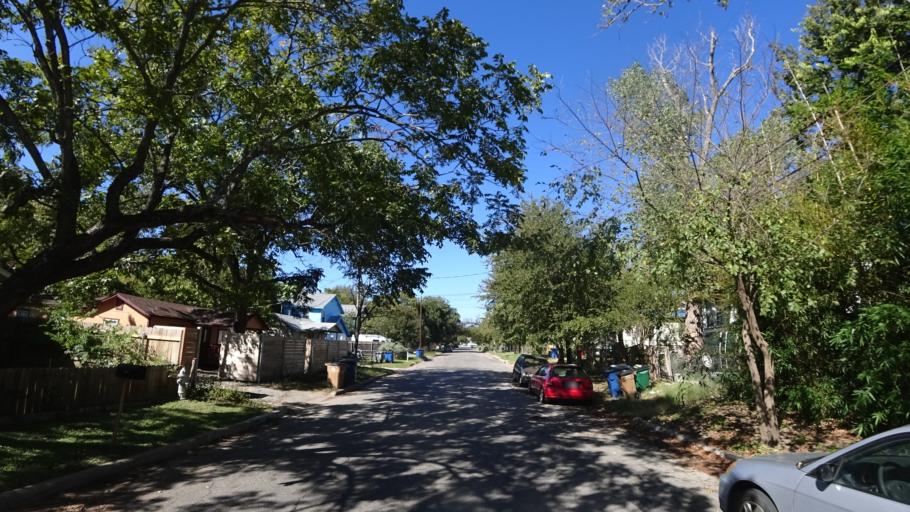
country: US
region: Texas
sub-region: Travis County
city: Austin
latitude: 30.2798
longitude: -97.6899
